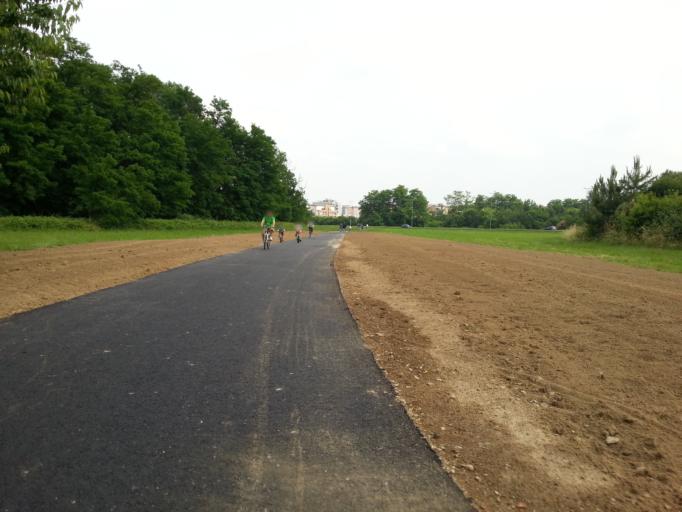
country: IT
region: Lombardy
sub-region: Citta metropolitana di Milano
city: Bresso
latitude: 45.5278
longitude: 9.1876
